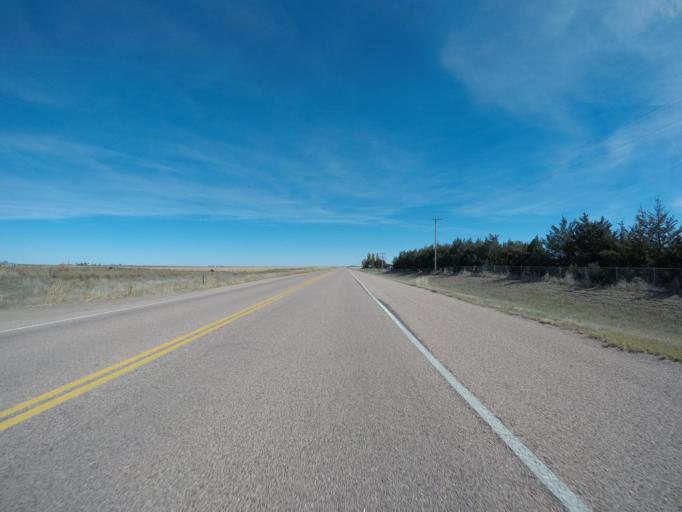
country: US
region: Colorado
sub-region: Yuma County
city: Yuma
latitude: 39.6560
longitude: -102.6267
